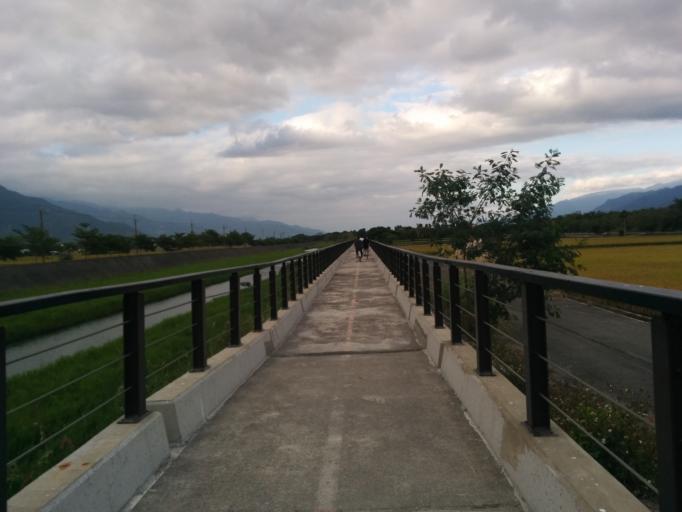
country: TW
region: Taiwan
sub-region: Taitung
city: Taitung
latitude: 23.0308
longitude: 121.1681
